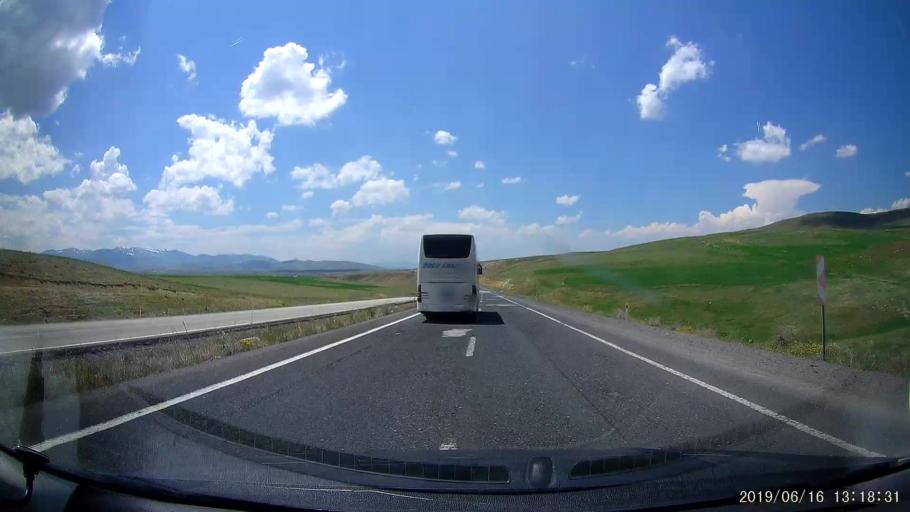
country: TR
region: Agri
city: Taslicay
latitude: 39.6309
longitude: 43.4292
